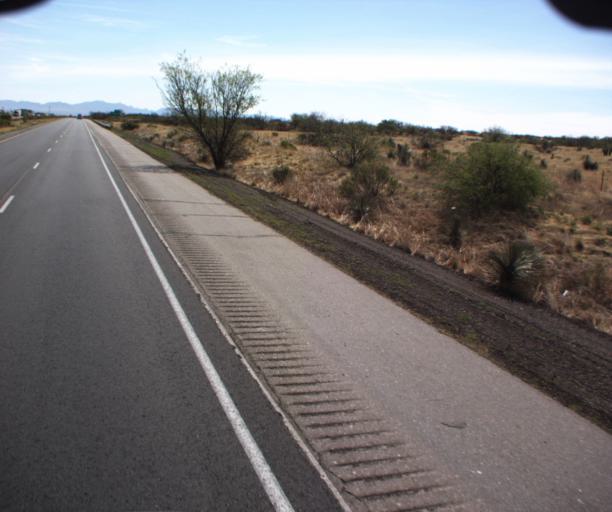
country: US
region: Arizona
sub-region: Cochise County
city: Mescal
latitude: 31.9629
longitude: -110.4133
